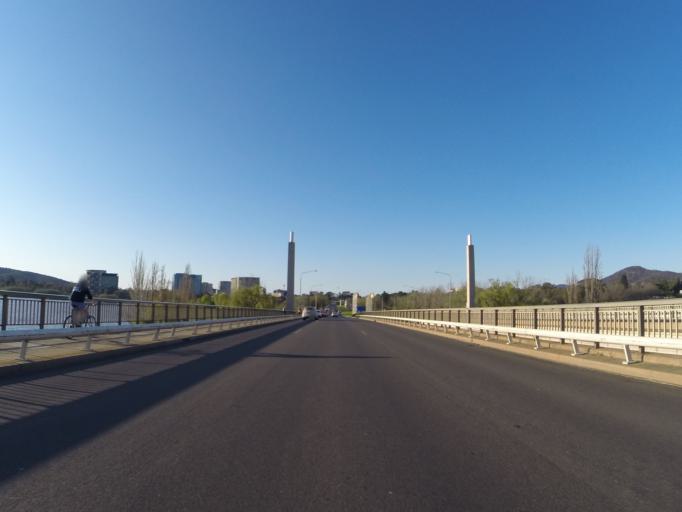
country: AU
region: Australian Capital Territory
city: Canberra
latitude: -35.2925
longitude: 149.1268
